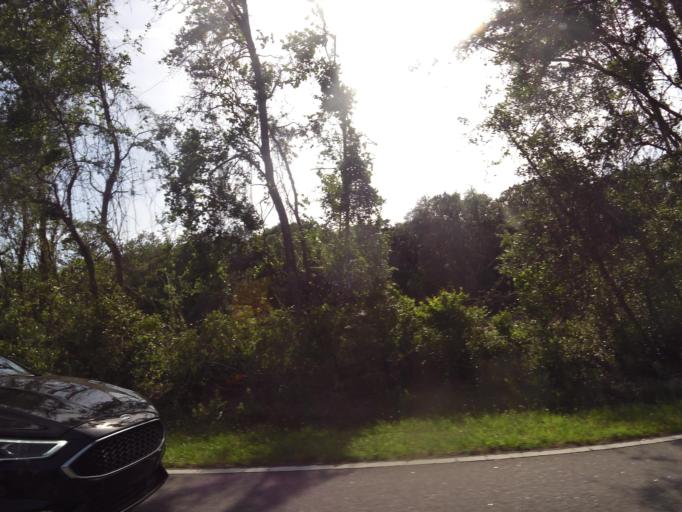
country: US
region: Florida
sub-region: Duval County
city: Atlantic Beach
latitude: 30.4932
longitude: -81.4719
